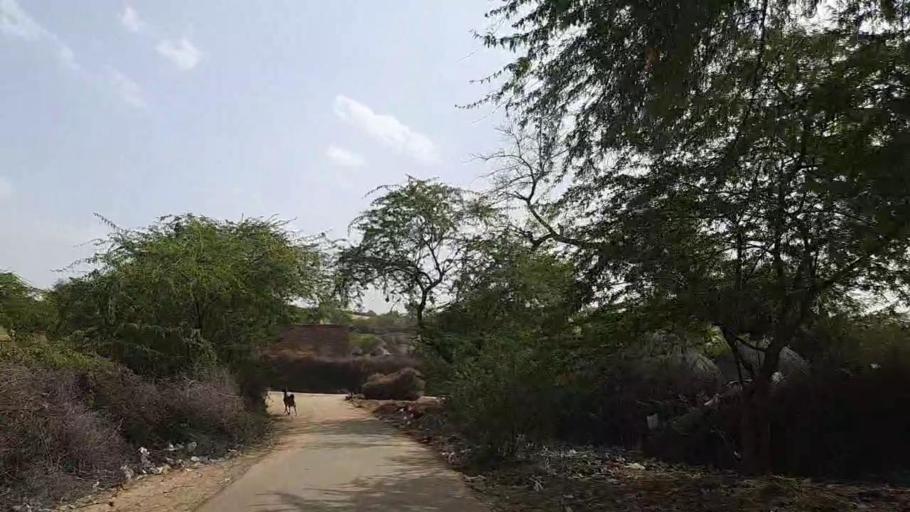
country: PK
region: Sindh
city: Islamkot
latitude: 24.8282
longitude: 70.1854
